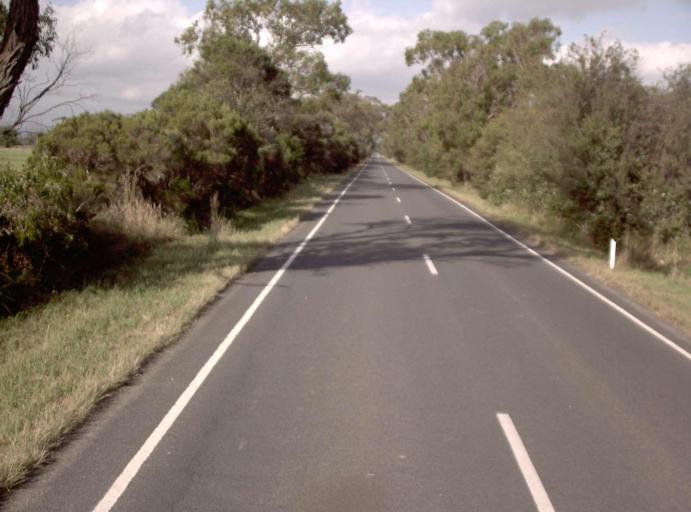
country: AU
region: Victoria
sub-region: Cardinia
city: Bunyip
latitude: -38.1502
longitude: 145.7360
